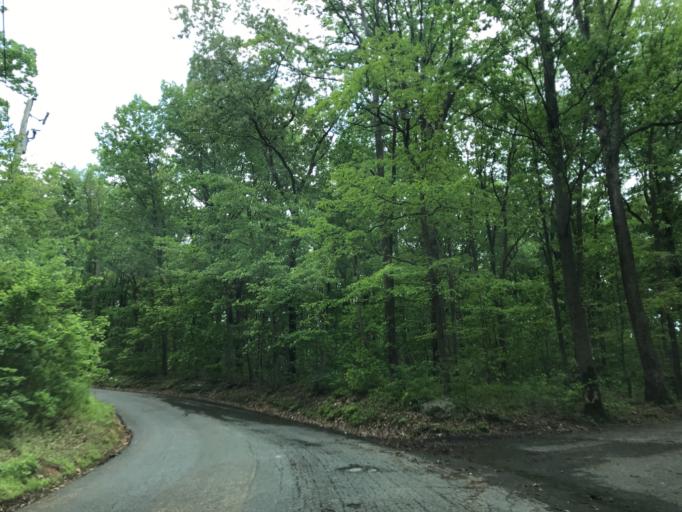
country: US
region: Pennsylvania
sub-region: York County
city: Susquehanna Trails
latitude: 39.6936
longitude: -76.3647
